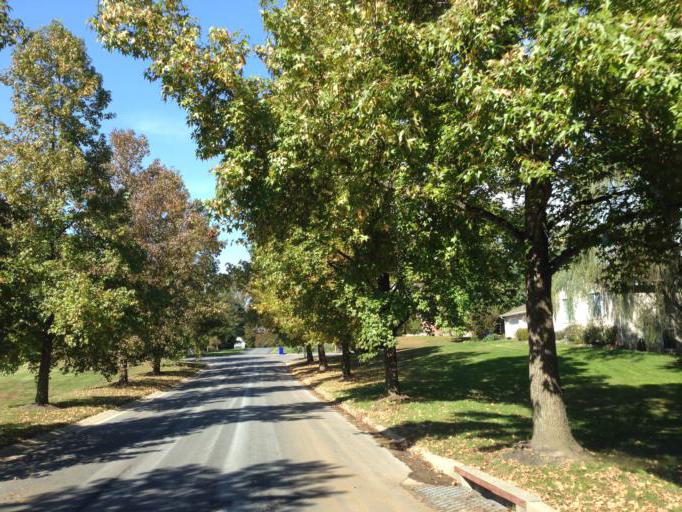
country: US
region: Maryland
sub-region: Howard County
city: Columbia
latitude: 39.2503
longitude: -76.8283
